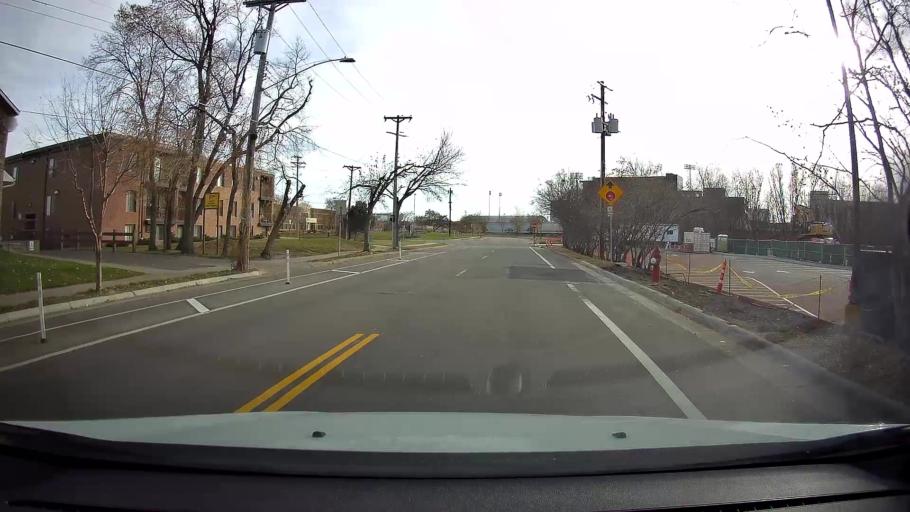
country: US
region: Minnesota
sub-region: Ramsey County
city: Lauderdale
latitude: 44.9851
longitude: -93.2287
